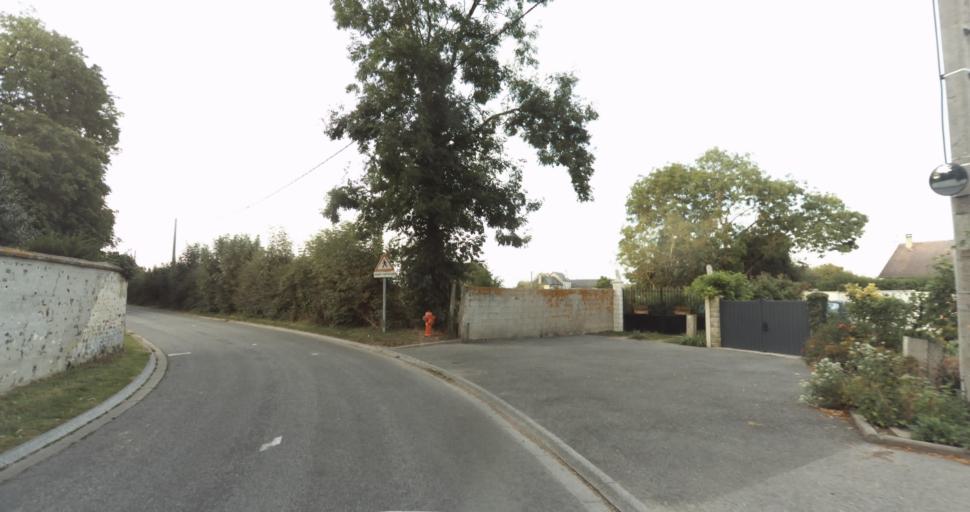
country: FR
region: Haute-Normandie
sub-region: Departement de l'Eure
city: Marcilly-sur-Eure
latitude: 48.8646
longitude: 1.2746
